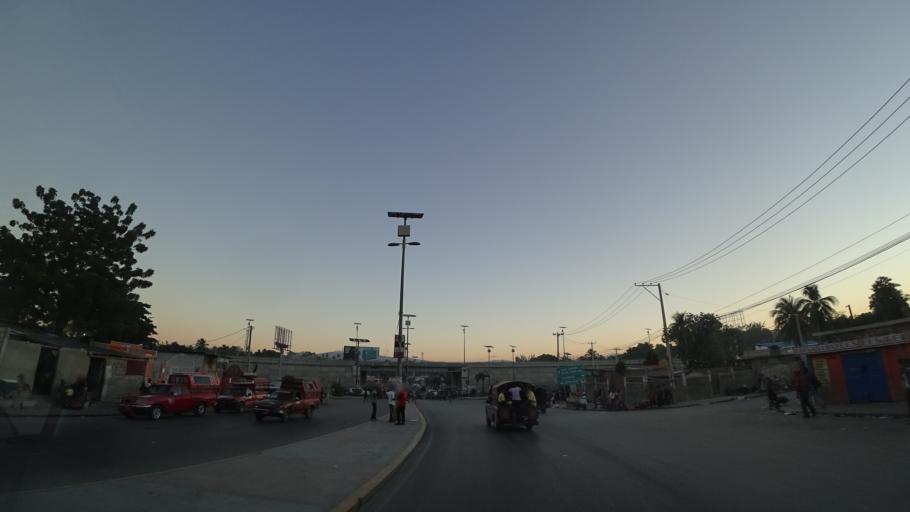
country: HT
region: Ouest
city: Delmas 73
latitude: 18.5523
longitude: -72.3154
